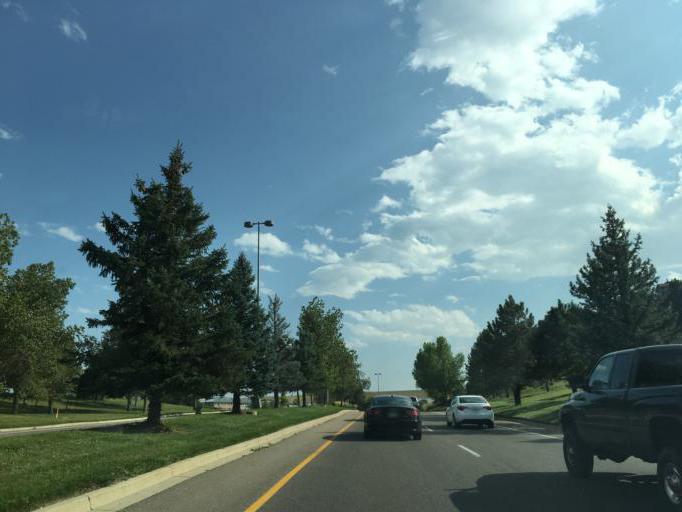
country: US
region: Colorado
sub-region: Broomfield County
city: Broomfield
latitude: 39.9261
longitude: -105.1279
